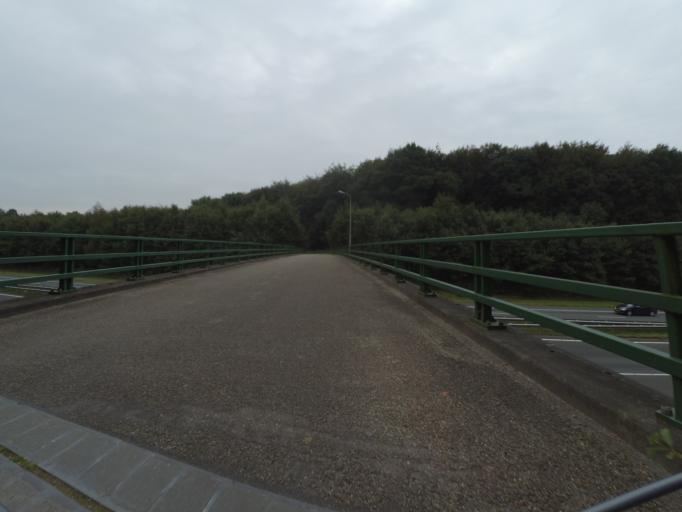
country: NL
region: Overijssel
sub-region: Gemeente Oldenzaal
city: Oldenzaal
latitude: 52.3057
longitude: 6.9785
